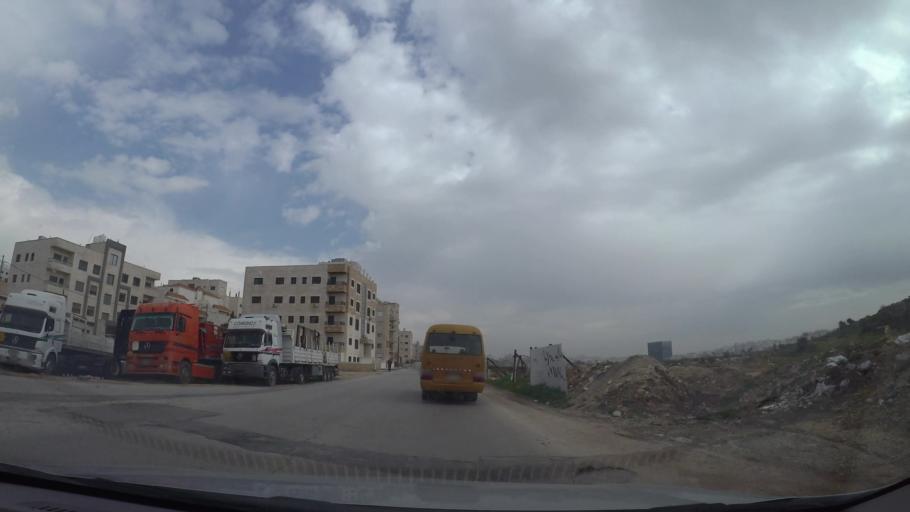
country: JO
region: Amman
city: Umm as Summaq
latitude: 31.8951
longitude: 35.8455
